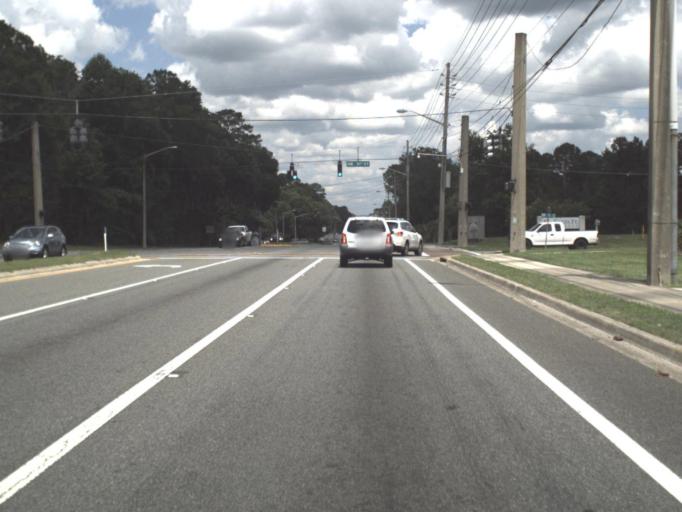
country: US
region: Florida
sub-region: Alachua County
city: Alachua
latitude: 29.6888
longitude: -82.4397
